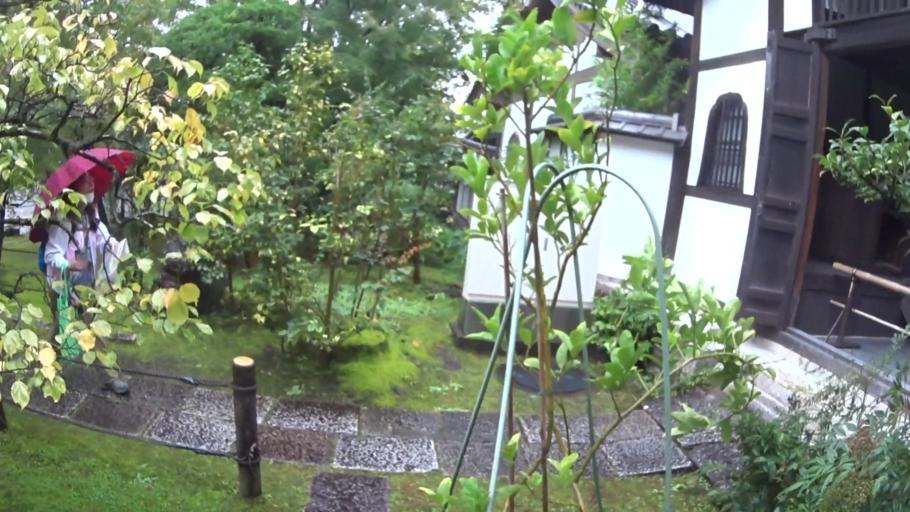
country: JP
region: Kyoto
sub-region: Kyoto-shi
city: Kamigyo-ku
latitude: 35.0146
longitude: 135.7951
